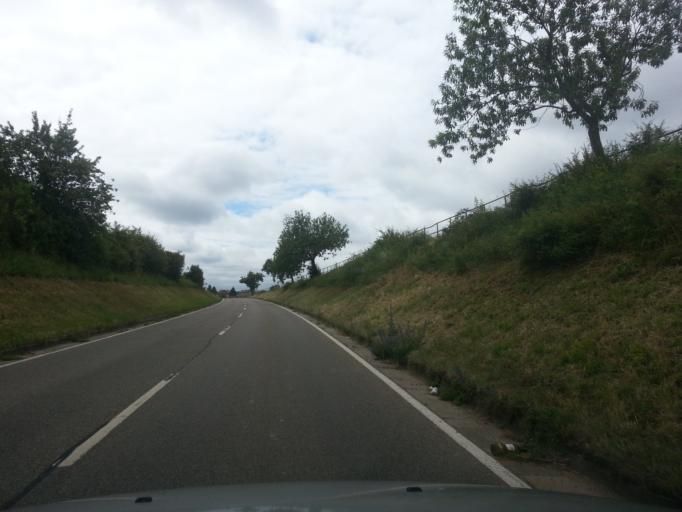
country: DE
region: Rheinland-Pfalz
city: Bobenheim am Berg
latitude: 49.5301
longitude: 8.1502
